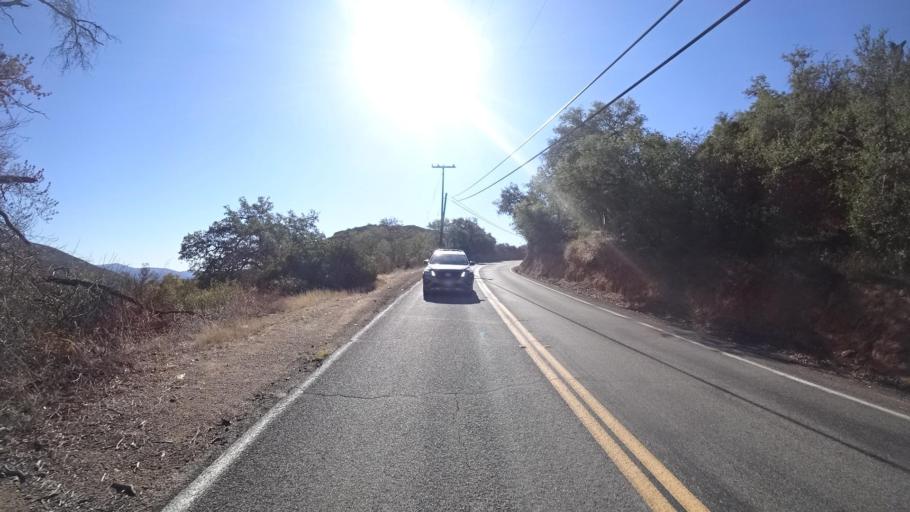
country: US
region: California
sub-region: San Diego County
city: Jamul
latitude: 32.7076
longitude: -116.7484
